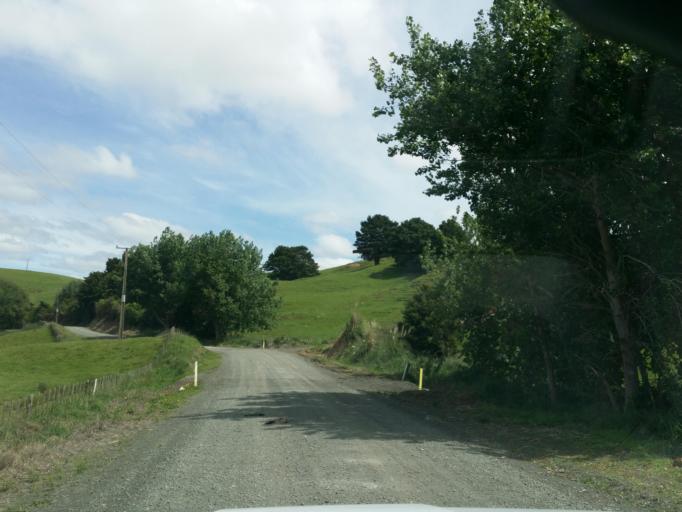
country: NZ
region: Northland
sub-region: Whangarei
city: Maungatapere
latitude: -35.9013
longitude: 174.1453
